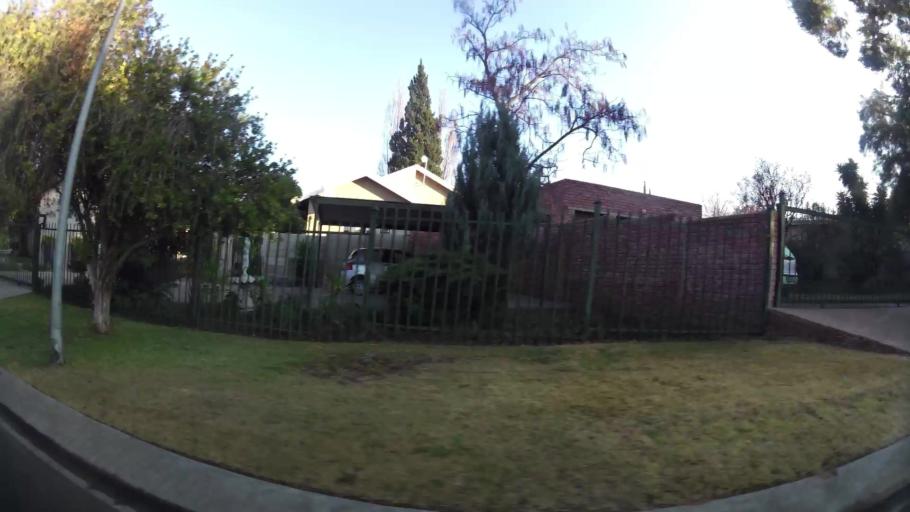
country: ZA
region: Orange Free State
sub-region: Mangaung Metropolitan Municipality
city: Bloemfontein
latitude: -29.1458
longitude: 26.1645
